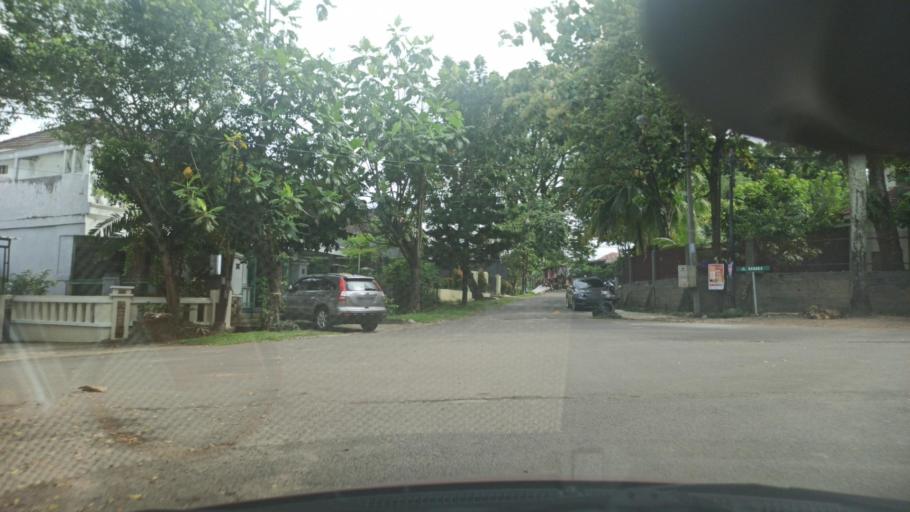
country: ID
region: South Sumatra
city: Plaju
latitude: -2.9868
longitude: 104.7396
